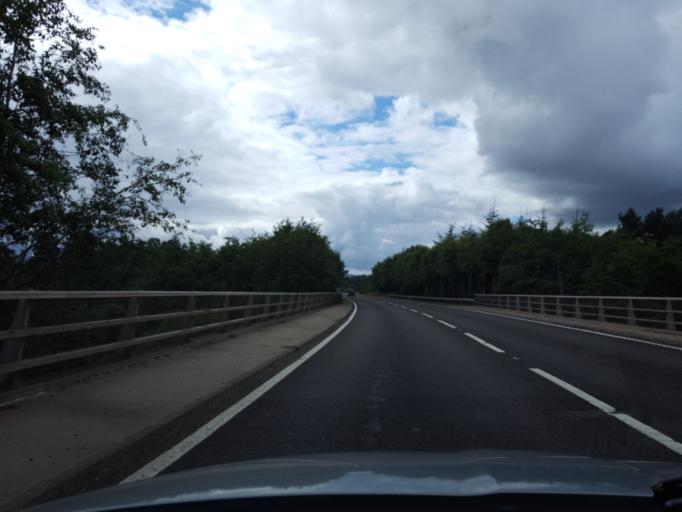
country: GB
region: Scotland
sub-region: Highland
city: Grantown on Spey
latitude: 57.3017
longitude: -3.6601
